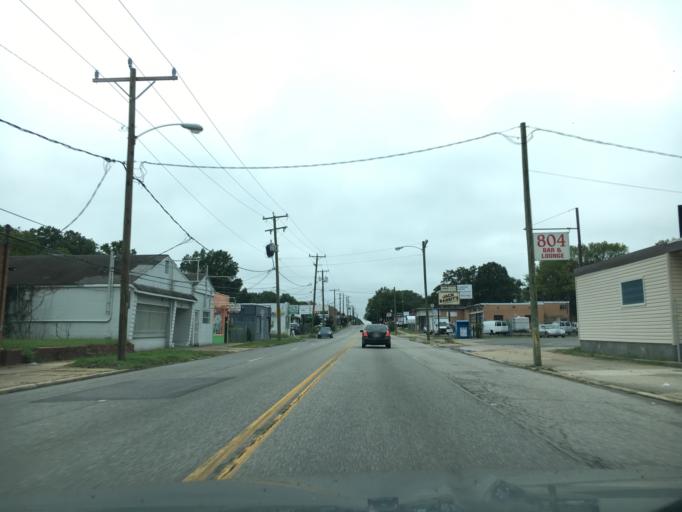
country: US
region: Virginia
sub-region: City of Richmond
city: Richmond
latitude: 37.5064
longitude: -77.4670
